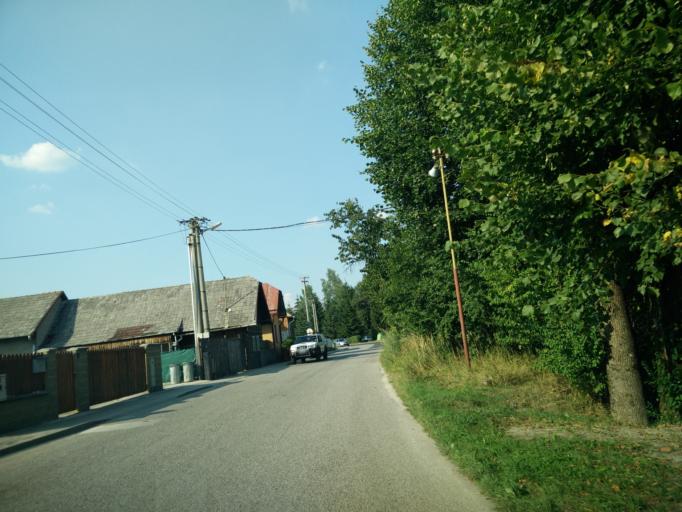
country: SK
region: Zilinsky
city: Rajec
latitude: 49.0704
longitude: 18.6289
